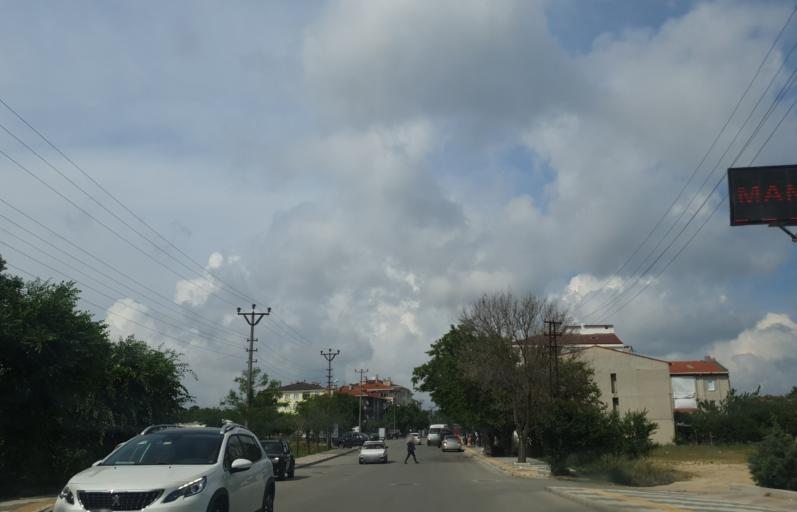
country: TR
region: Tekirdag
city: Saray
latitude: 41.4483
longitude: 27.9304
